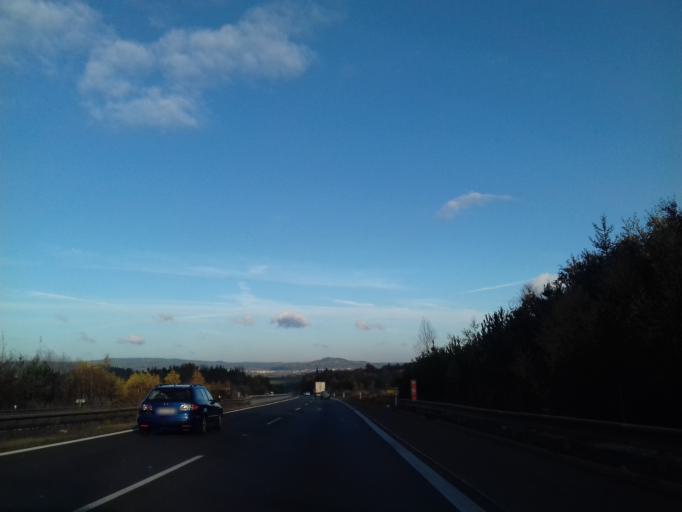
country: CZ
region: Plzensky
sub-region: Okres Rokycany
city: Rokycany
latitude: 49.7423
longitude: 13.5424
